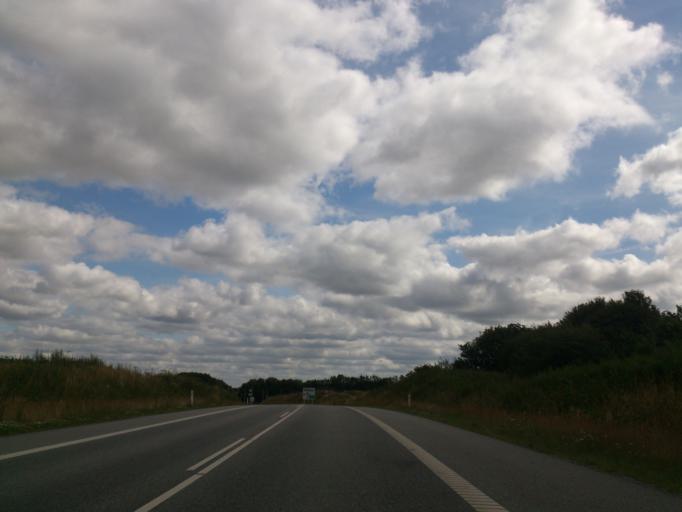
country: DK
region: South Denmark
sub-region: Aabenraa Kommune
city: Aabenraa
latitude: 54.9488
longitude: 9.4492
